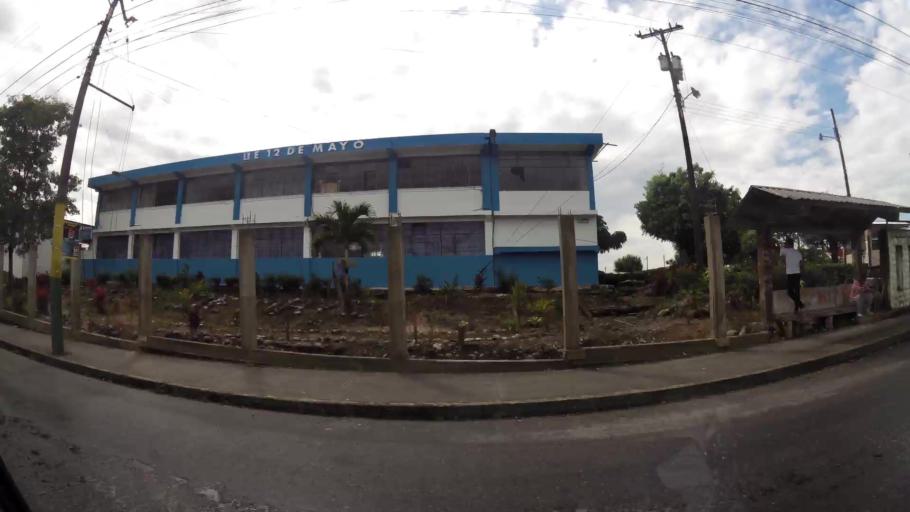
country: EC
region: Pastaza
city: Puyo
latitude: -1.4924
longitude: -77.9972
